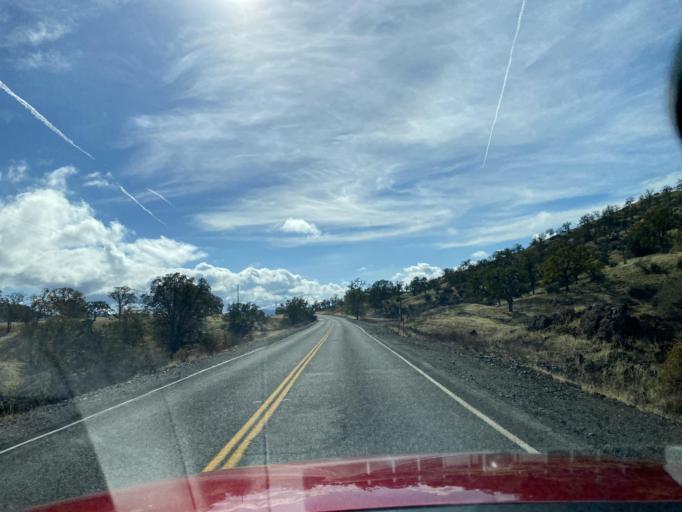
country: US
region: California
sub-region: Glenn County
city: Willows
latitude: 39.4783
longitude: -122.5147
